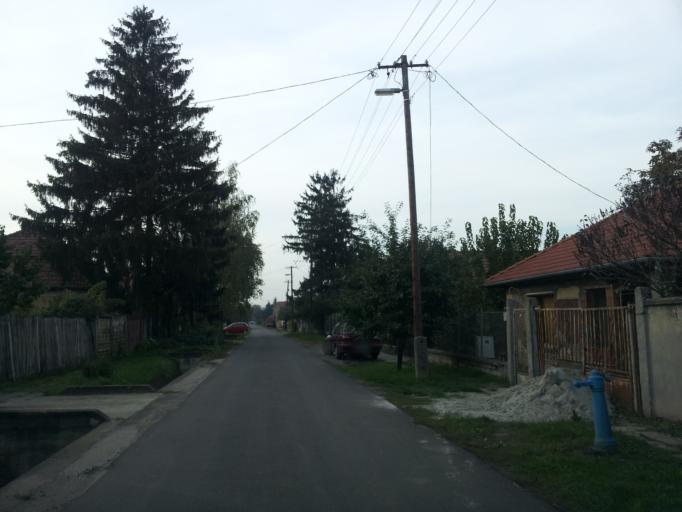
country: HU
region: Pest
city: Nagykata
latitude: 47.4240
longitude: 19.7414
